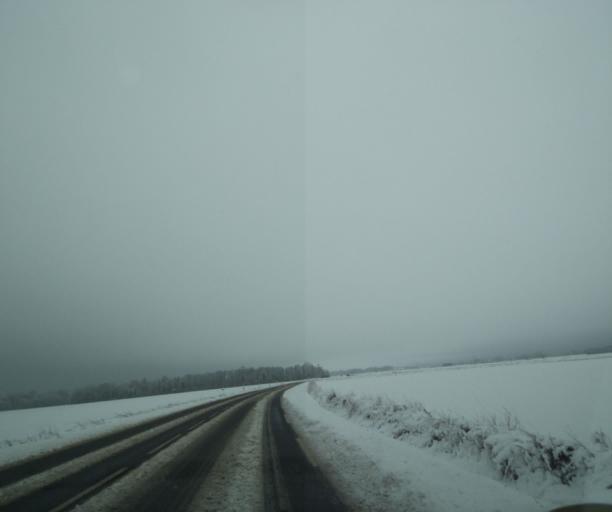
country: FR
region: Champagne-Ardenne
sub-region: Departement de la Haute-Marne
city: Wassy
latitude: 48.5659
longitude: 4.9214
